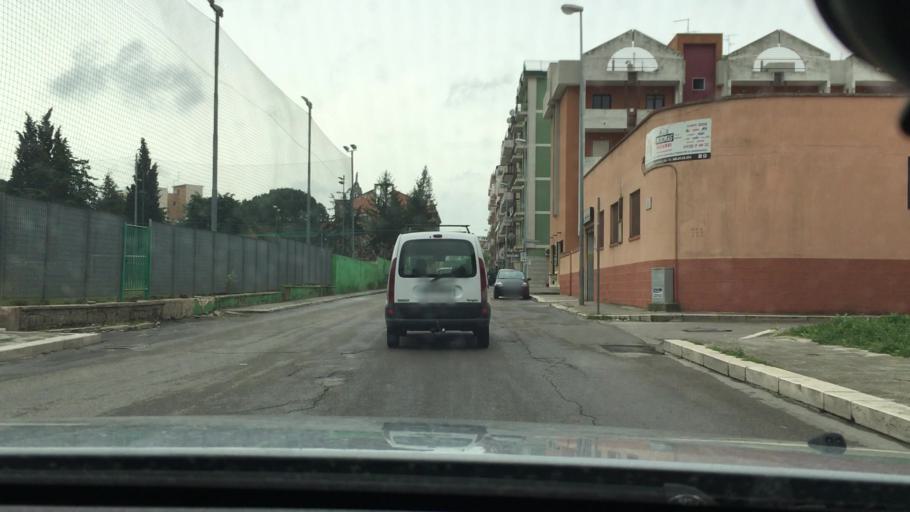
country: IT
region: Apulia
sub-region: Provincia di Bari
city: Gioia del Colle
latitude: 40.8057
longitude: 16.9240
